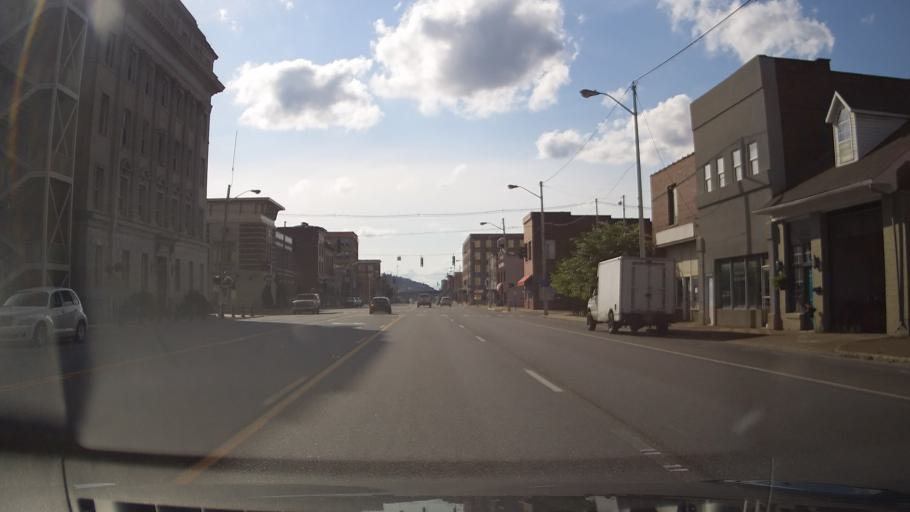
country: US
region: Kentucky
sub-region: Boyd County
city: Ashland
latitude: 38.4787
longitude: -82.6369
